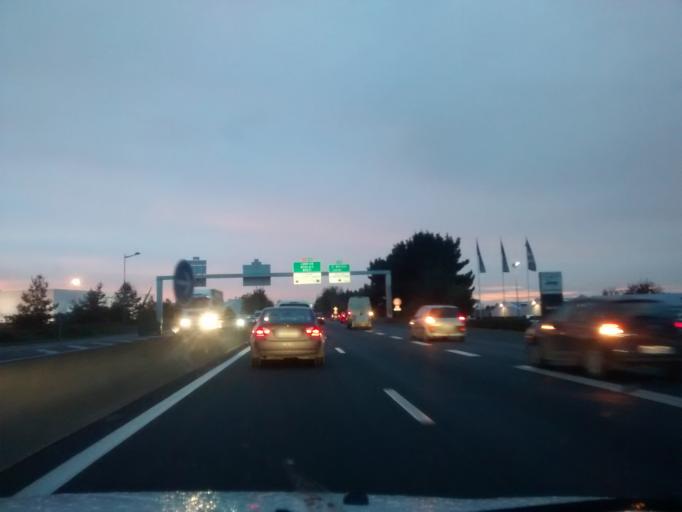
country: FR
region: Brittany
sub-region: Departement des Cotes-d'Armor
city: Langueux
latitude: 48.5068
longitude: -2.7352
